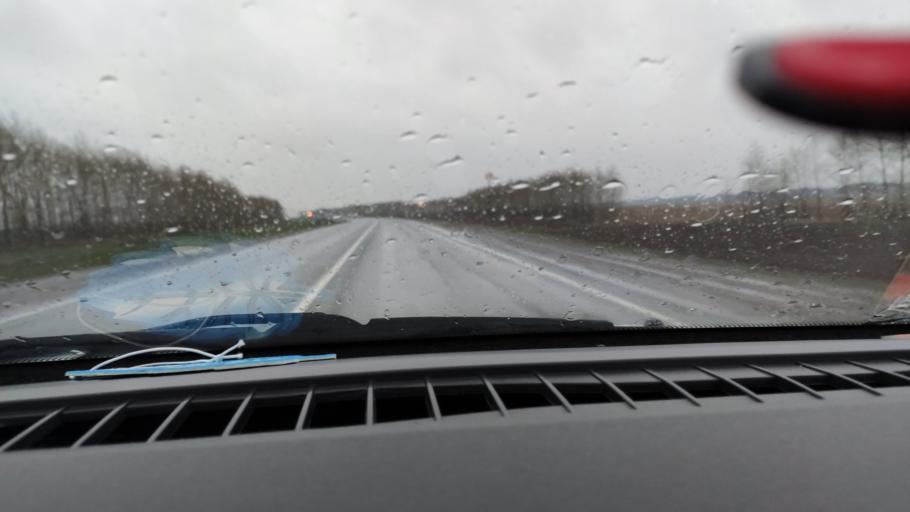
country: RU
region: Tatarstan
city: Mendeleyevsk
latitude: 55.9234
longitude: 52.2760
